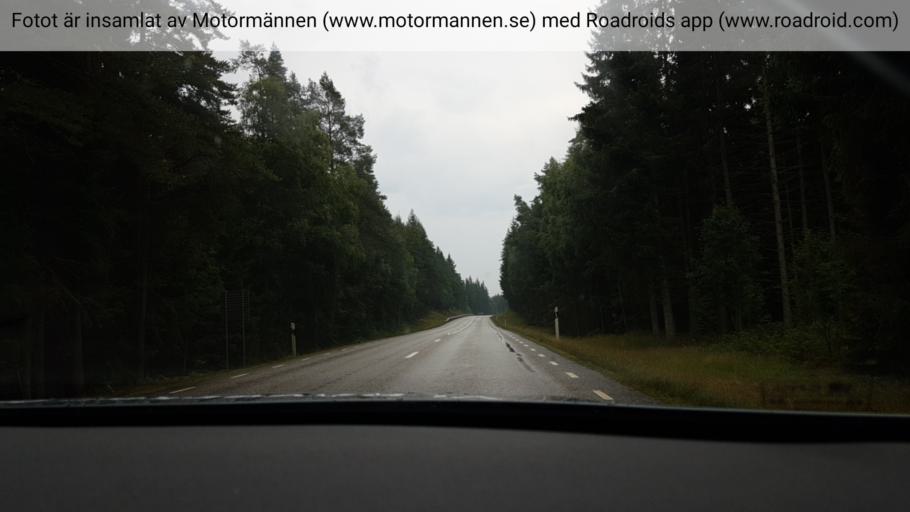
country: SE
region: Joenkoeping
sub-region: Vaggeryds Kommun
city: Vaggeryd
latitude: 57.5599
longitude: 14.2555
